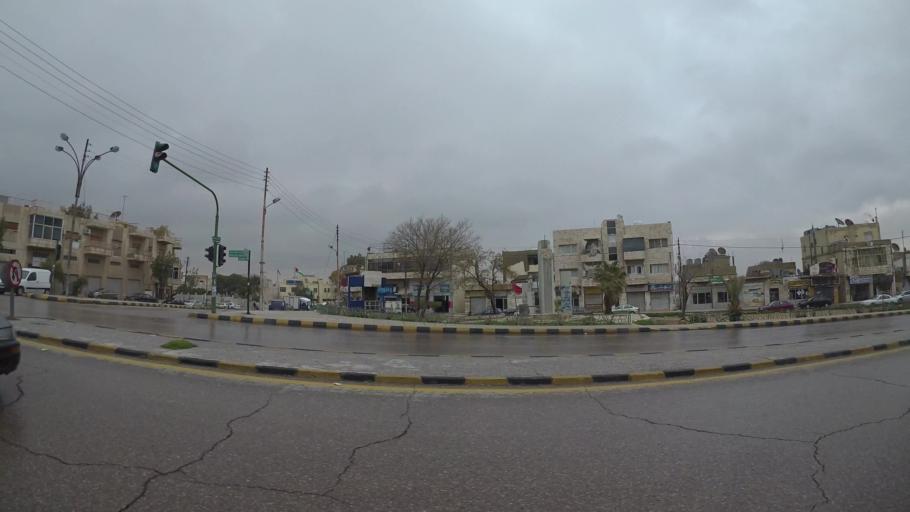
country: JO
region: Amman
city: Amman
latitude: 31.9597
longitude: 35.9314
